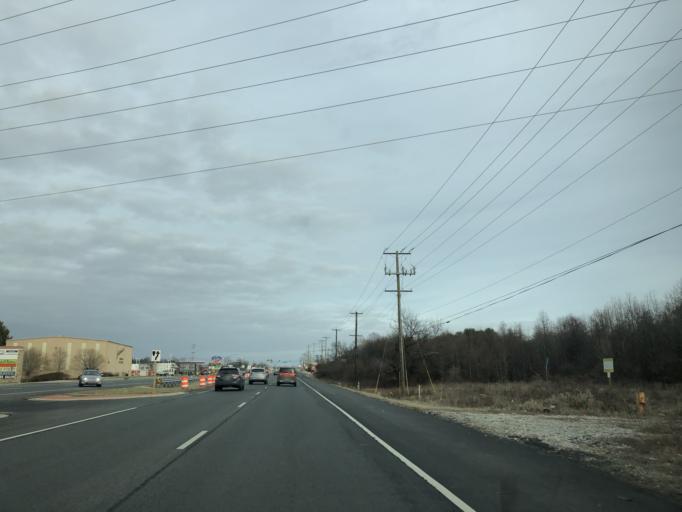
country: US
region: Maryland
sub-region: Cecil County
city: Elkton
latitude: 39.5999
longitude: -75.8074
